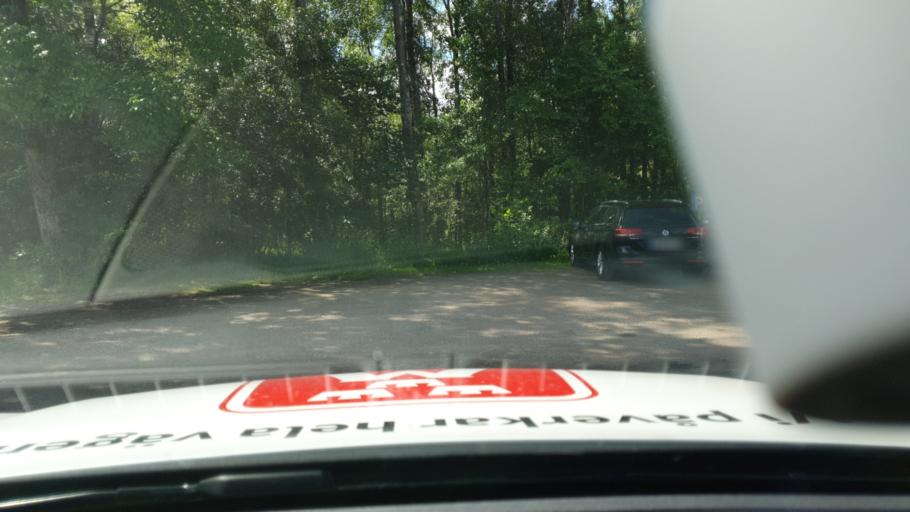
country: SE
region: Vaestra Goetaland
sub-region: Falkopings Kommun
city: Falkoeping
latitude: 58.1376
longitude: 13.6002
